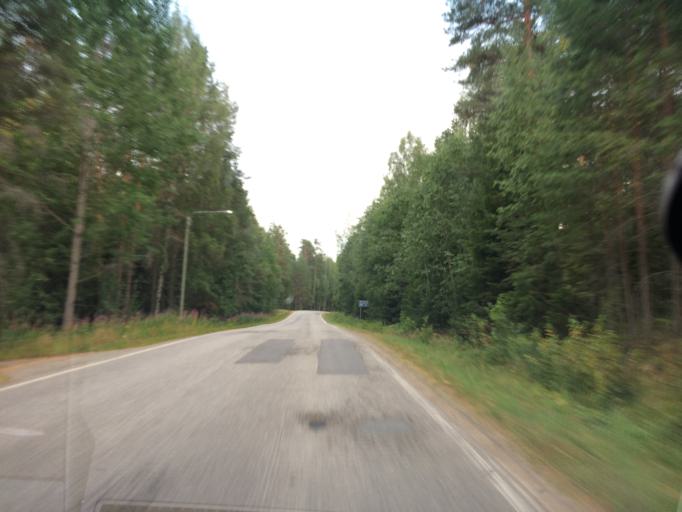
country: FI
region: Pirkanmaa
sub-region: Tampere
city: Luopioinen
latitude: 61.2499
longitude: 24.7074
